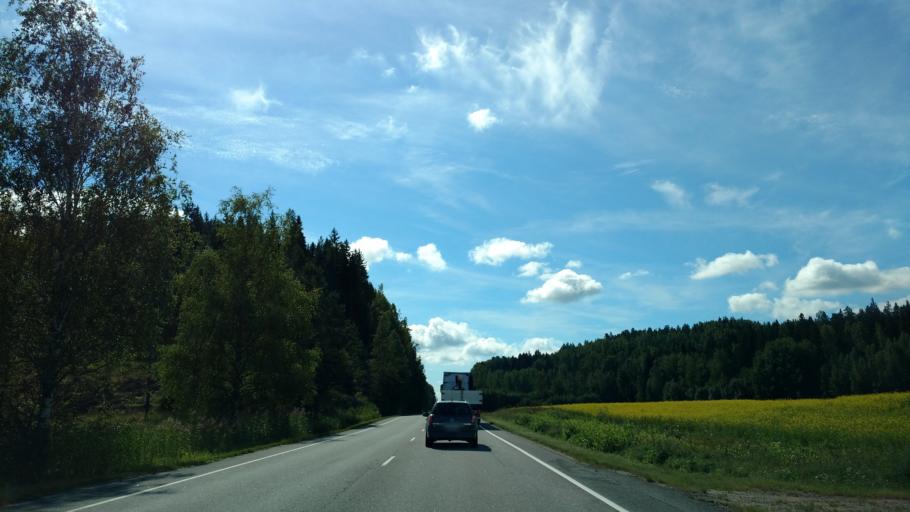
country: FI
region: Varsinais-Suomi
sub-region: Salo
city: Salo
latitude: 60.3129
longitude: 23.0992
